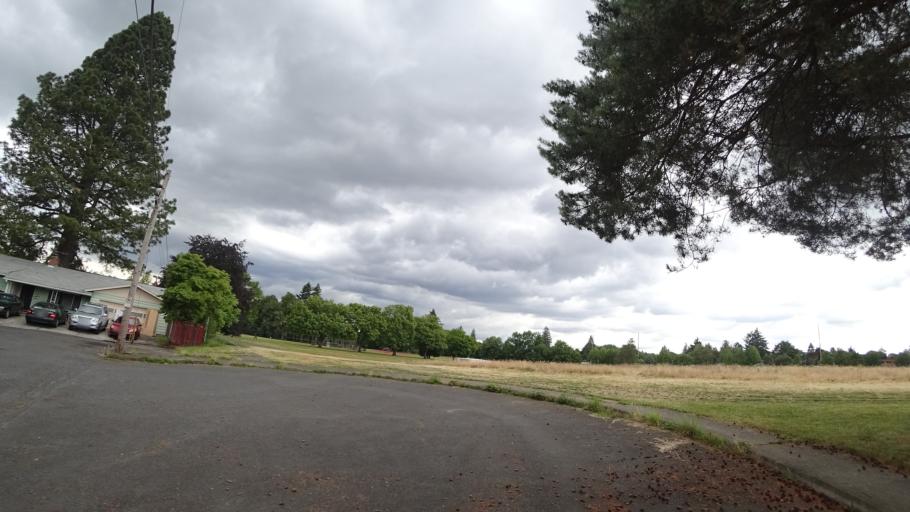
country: US
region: Oregon
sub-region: Multnomah County
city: Portland
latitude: 45.5644
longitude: -122.6234
